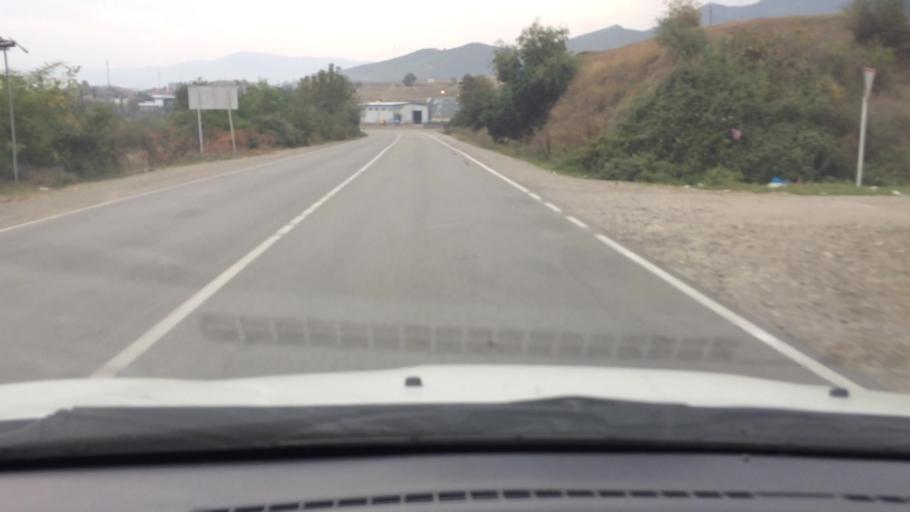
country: AM
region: Tavush
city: Bagratashen
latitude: 41.2292
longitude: 44.8236
